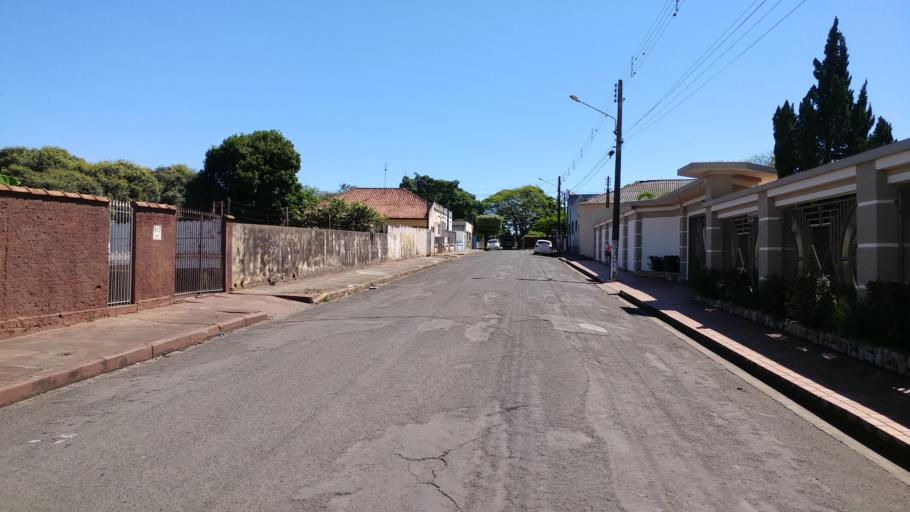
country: BR
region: Sao Paulo
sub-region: Paraguacu Paulista
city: Paraguacu Paulista
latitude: -22.4185
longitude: -50.5778
